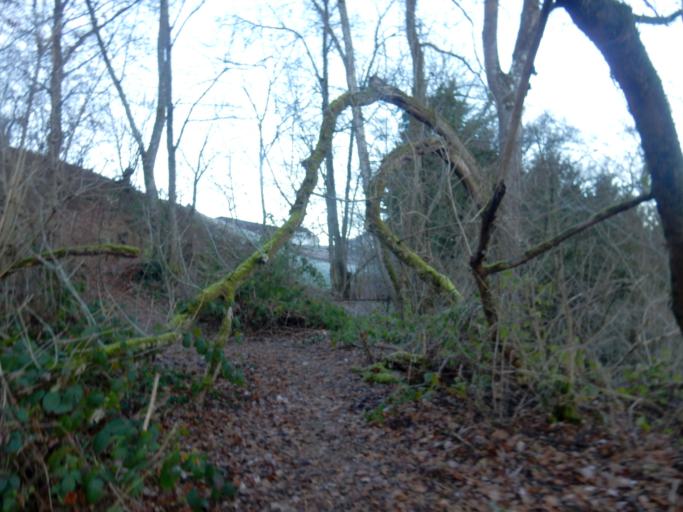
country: LU
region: Diekirch
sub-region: Canton de Diekirch
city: Bourscheid
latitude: 49.9195
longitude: 6.0681
